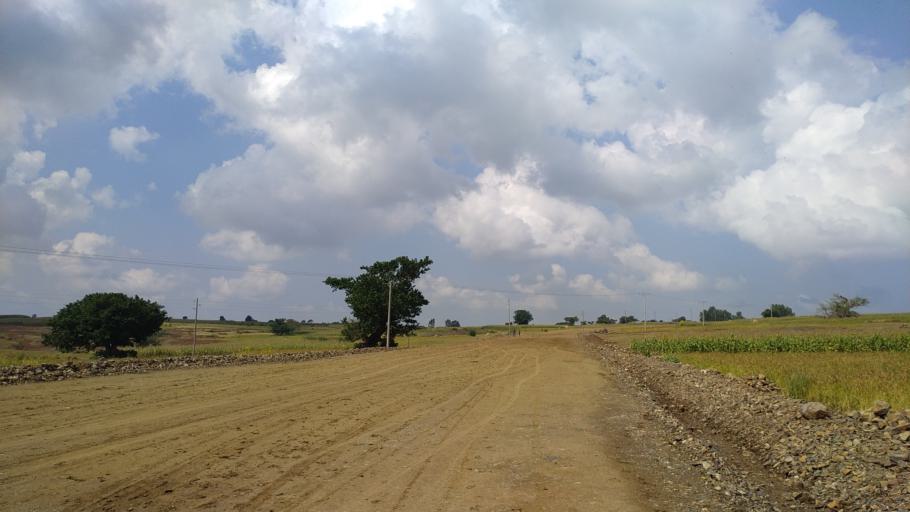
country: ET
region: Amhara
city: Werota
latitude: 11.7685
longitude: 37.5853
